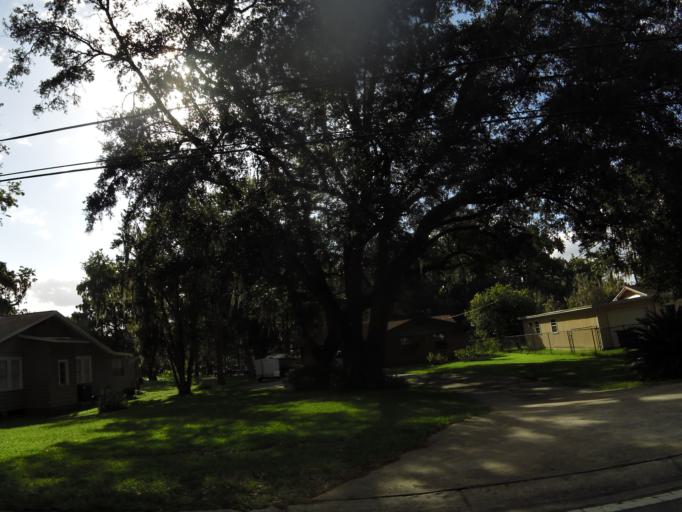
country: US
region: Florida
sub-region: Duval County
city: Jacksonville
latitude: 30.2871
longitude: -81.7388
